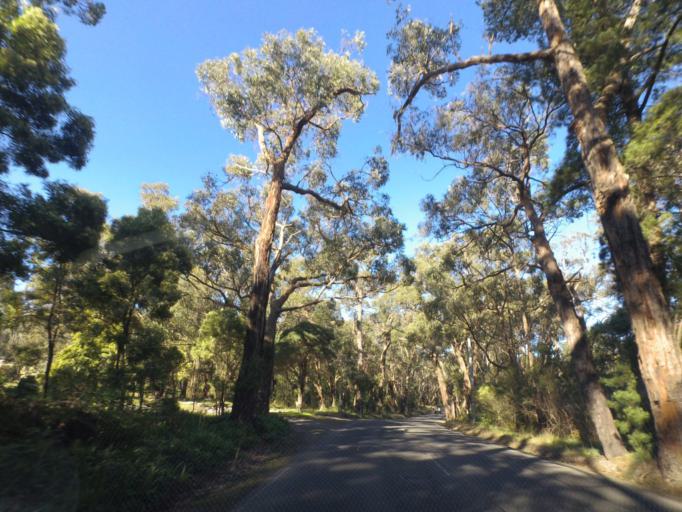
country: AU
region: Victoria
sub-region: Yarra Ranges
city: Montrose
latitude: -37.8016
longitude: 145.3412
